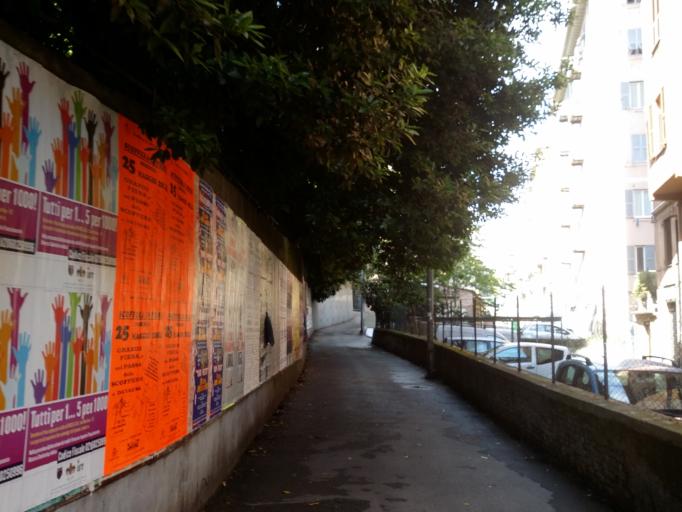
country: IT
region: Liguria
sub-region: Provincia di Genova
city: Genoa
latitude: 44.4076
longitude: 8.9611
